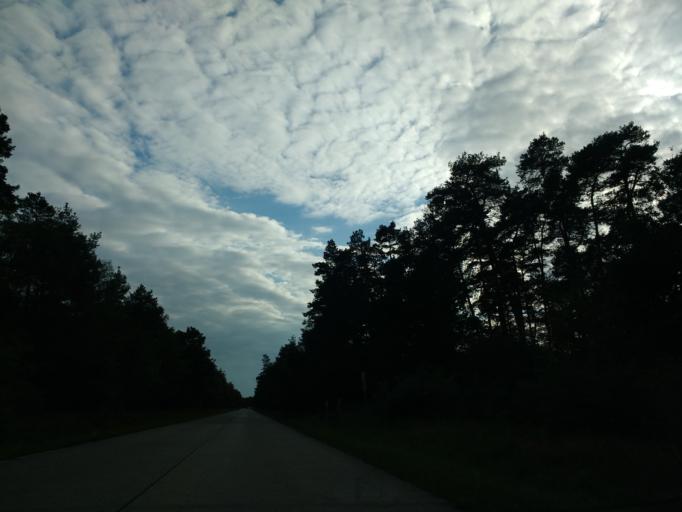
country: DE
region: North Rhine-Westphalia
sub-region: Regierungsbezirk Detmold
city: Augustdorf
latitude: 51.8738
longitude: 8.7023
